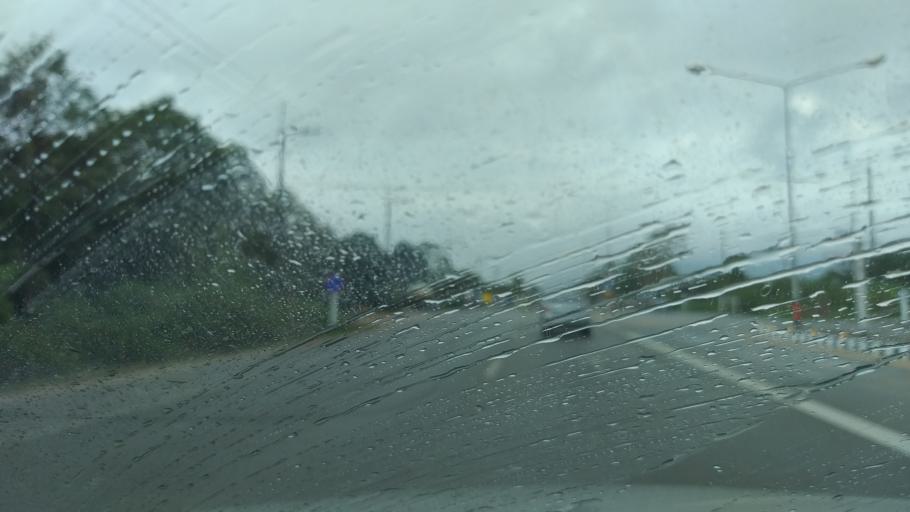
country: TH
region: Chanthaburi
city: Khlung
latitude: 12.4524
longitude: 102.2425
